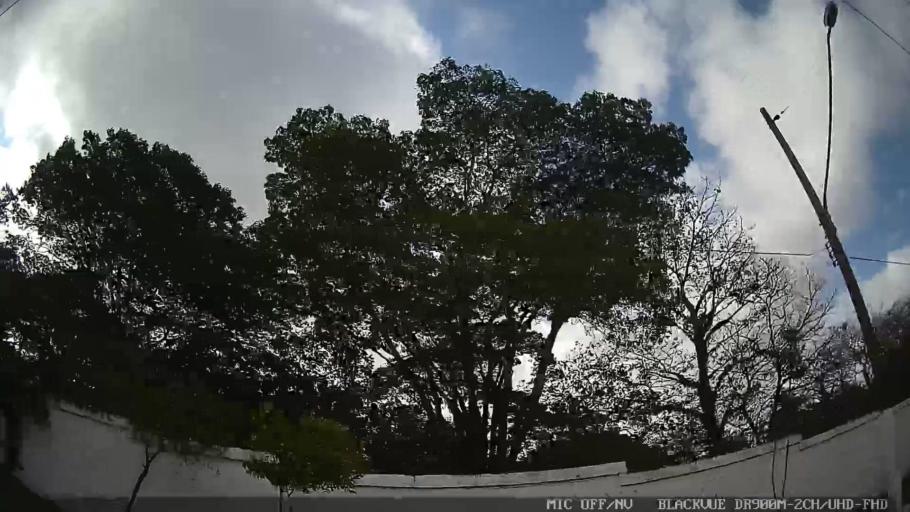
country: BR
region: Sao Paulo
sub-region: Sao Caetano Do Sul
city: Sao Caetano do Sul
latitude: -23.5647
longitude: -46.5240
